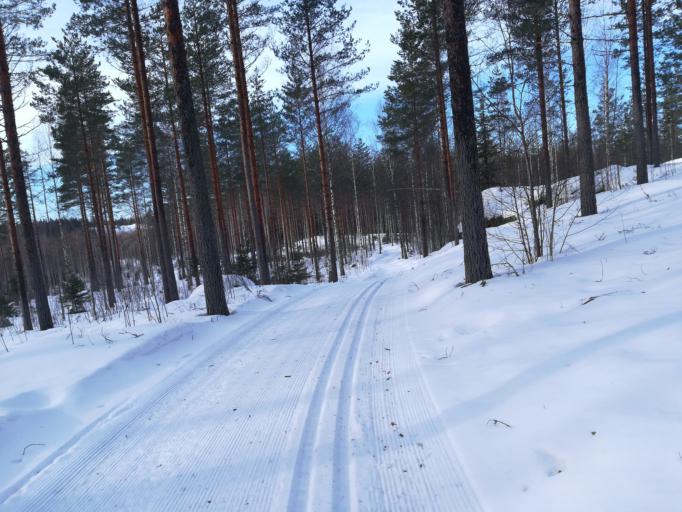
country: FI
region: Southern Savonia
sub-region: Savonlinna
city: Savonlinna
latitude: 61.8073
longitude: 29.0518
